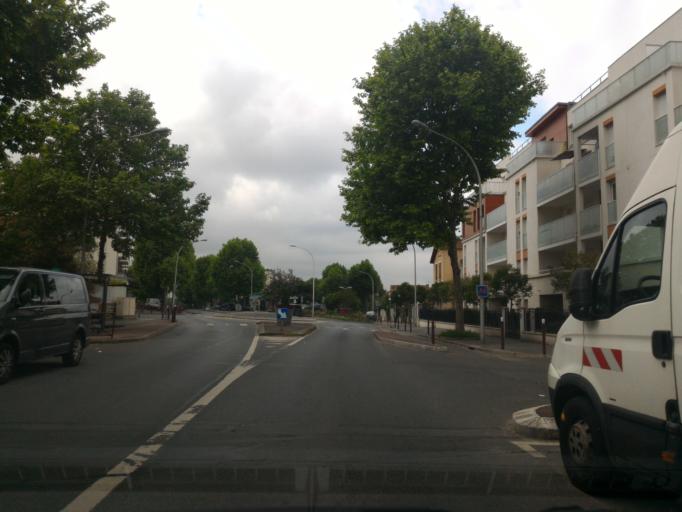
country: FR
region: Ile-de-France
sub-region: Departement du Val-de-Marne
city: L'Hay-les-Roses
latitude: 48.7849
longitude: 2.3415
